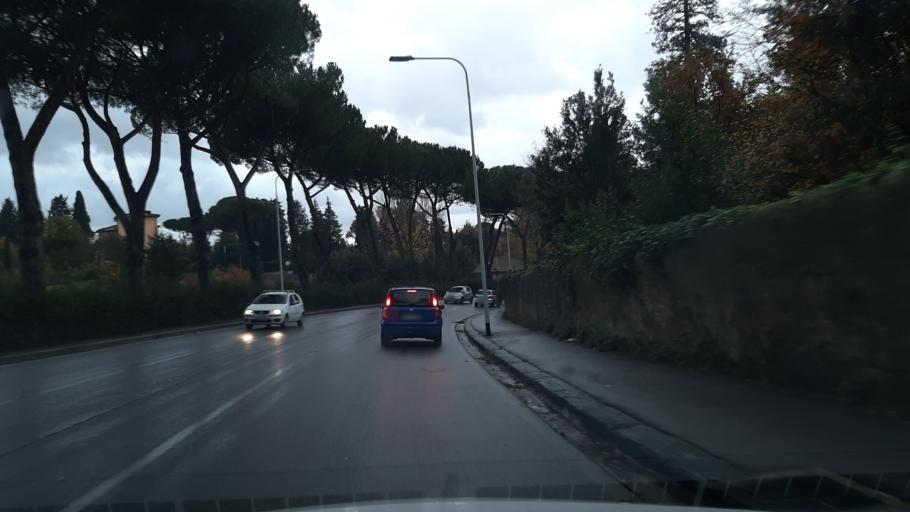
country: IT
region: Tuscany
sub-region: Province of Florence
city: Florence
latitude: 43.8093
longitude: 11.2507
